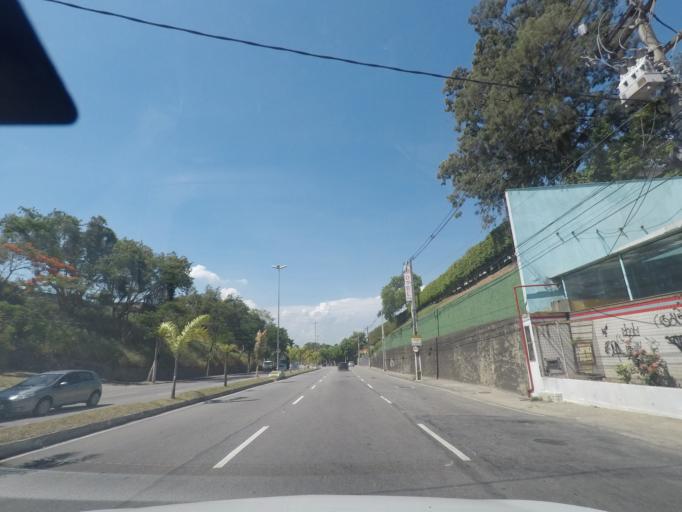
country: BR
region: Rio de Janeiro
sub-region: Niteroi
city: Niteroi
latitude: -22.9158
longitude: -43.0485
